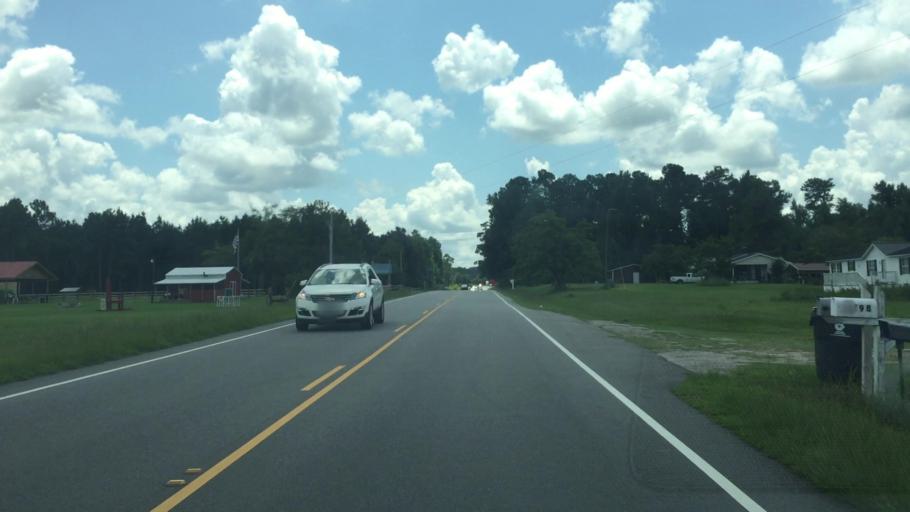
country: US
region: North Carolina
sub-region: Columbus County
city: Chadbourn
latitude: 34.2530
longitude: -78.8186
